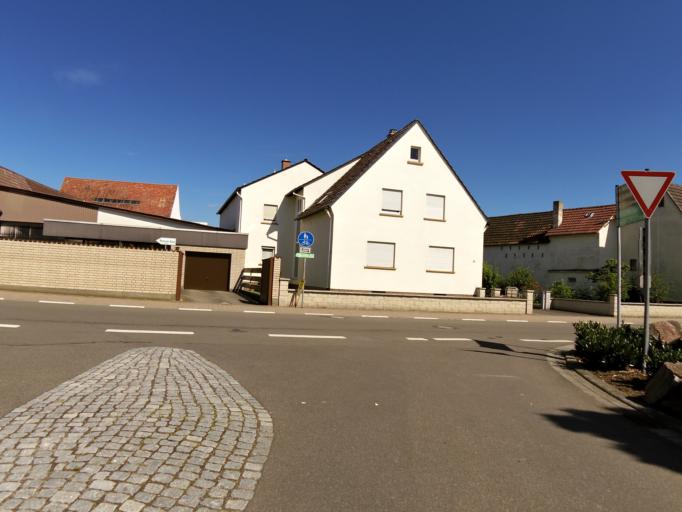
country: DE
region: Rheinland-Pfalz
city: Harthausen
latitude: 49.2973
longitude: 8.3435
